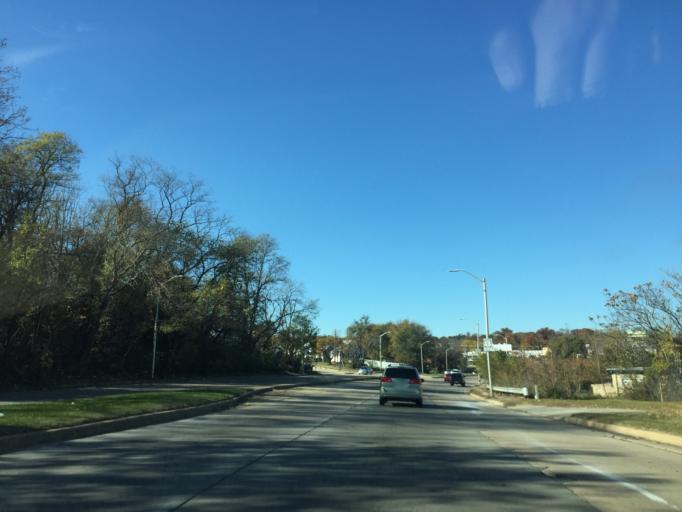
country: US
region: Maryland
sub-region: Baltimore County
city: Lansdowne
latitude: 39.2558
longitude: -76.6600
